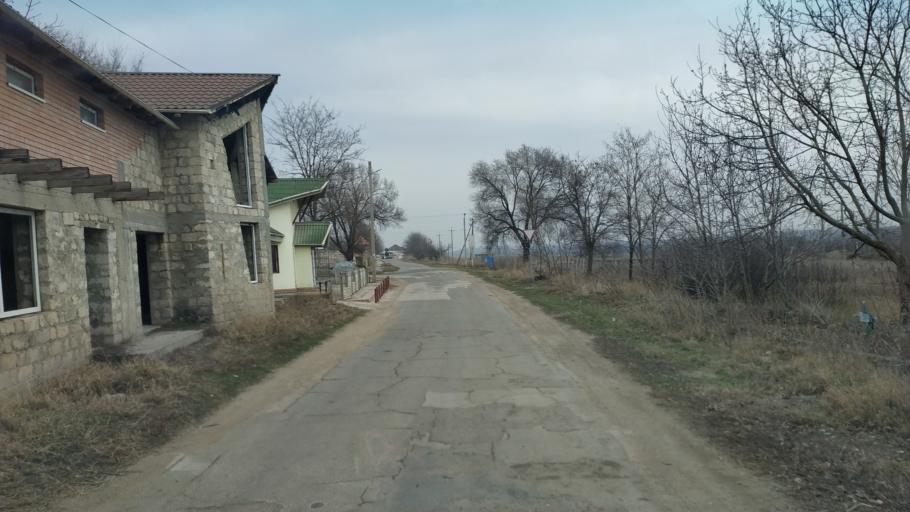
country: MD
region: Chisinau
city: Singera
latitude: 46.9331
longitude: 28.9805
